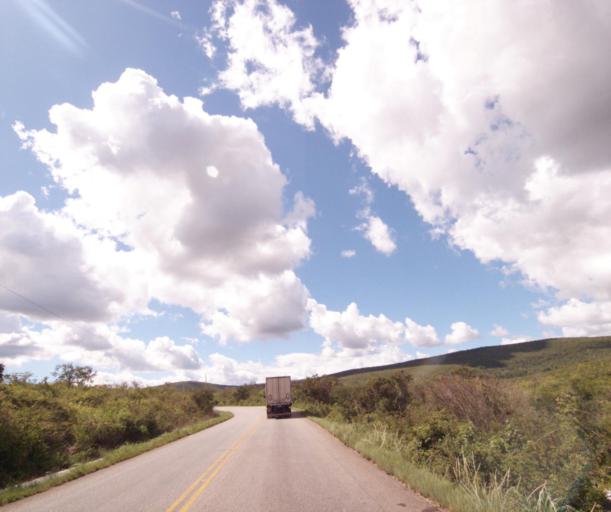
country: BR
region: Bahia
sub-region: Caetite
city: Caetite
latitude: -14.1488
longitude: -42.3572
